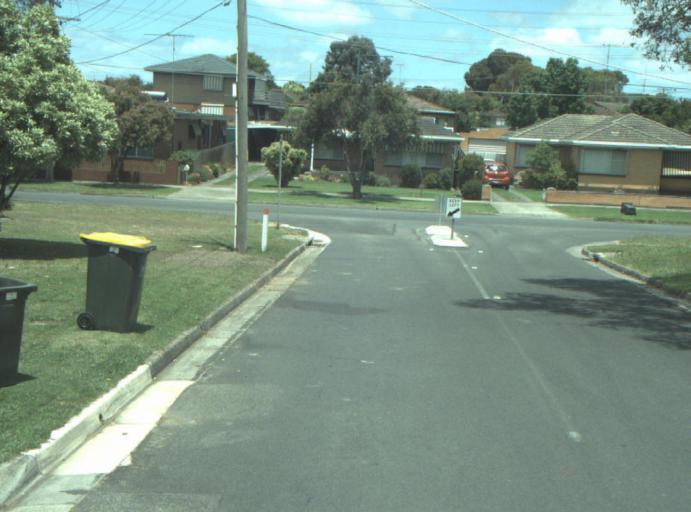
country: AU
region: Victoria
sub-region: Greater Geelong
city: Breakwater
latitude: -38.1850
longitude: 144.3422
